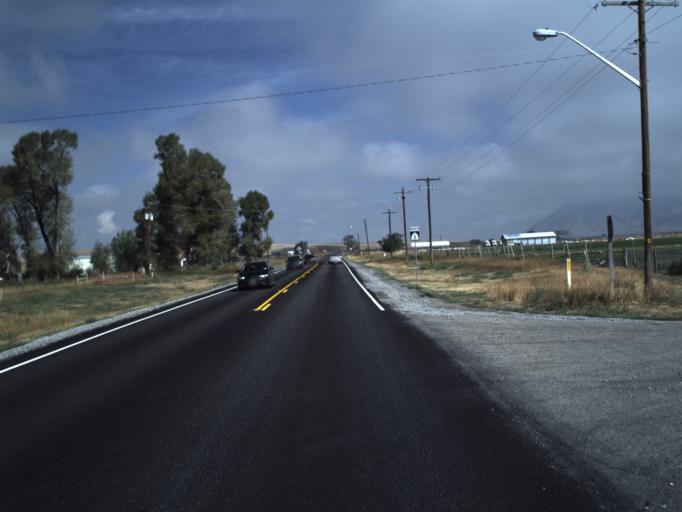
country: US
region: Utah
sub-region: Rich County
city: Randolph
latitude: 41.5262
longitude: -111.1629
